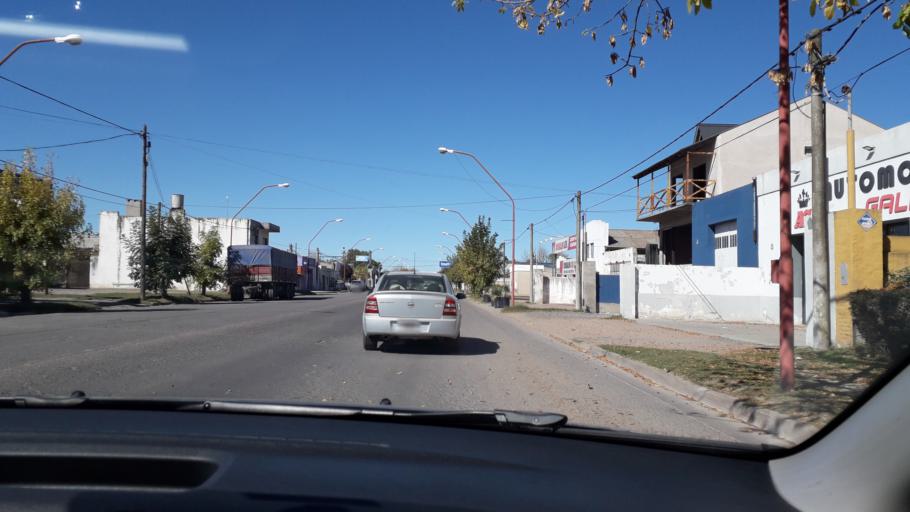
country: AR
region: Buenos Aires
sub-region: Partido de Azul
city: Azul
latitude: -36.7888
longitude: -59.8447
